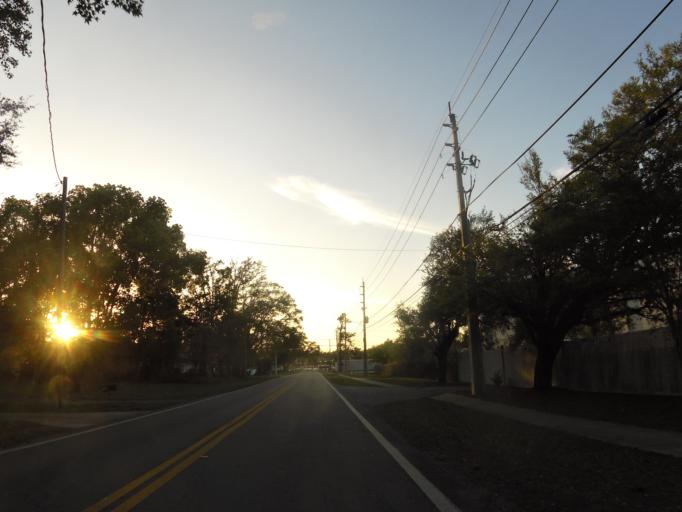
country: US
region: Florida
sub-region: Duval County
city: Jacksonville
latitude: 30.2881
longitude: -81.5837
